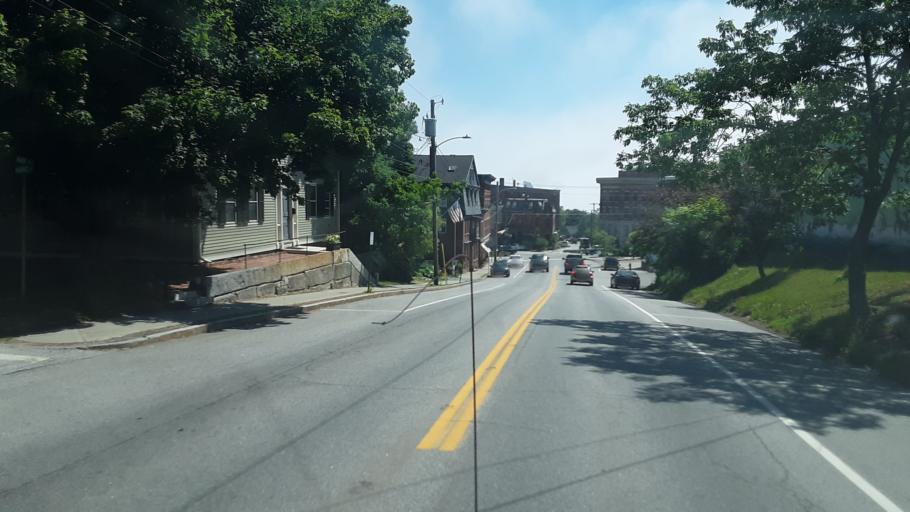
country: US
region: Maine
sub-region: Waldo County
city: Belfast
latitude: 44.4253
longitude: -69.0091
